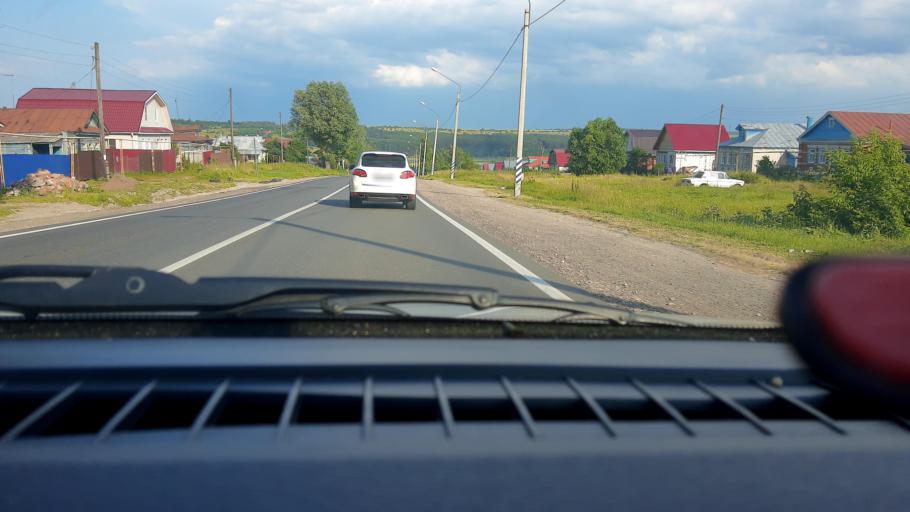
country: RU
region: Nizjnij Novgorod
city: Dal'neye Konstantinovo
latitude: 55.8252
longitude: 43.9914
